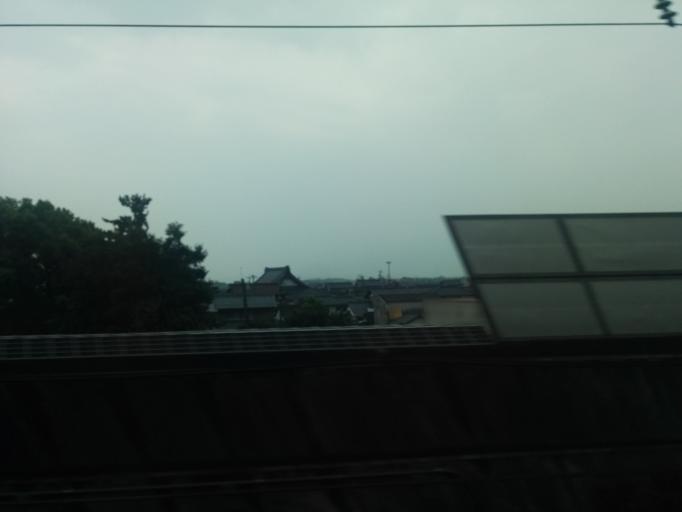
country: JP
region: Aichi
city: Sobue
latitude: 35.2981
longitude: 136.7179
